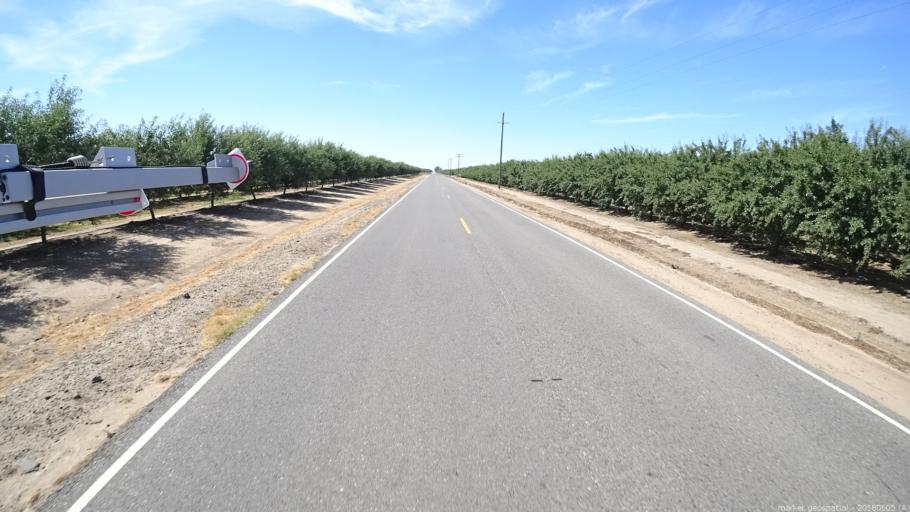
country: US
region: California
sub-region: Madera County
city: Chowchilla
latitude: 37.0564
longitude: -120.3830
